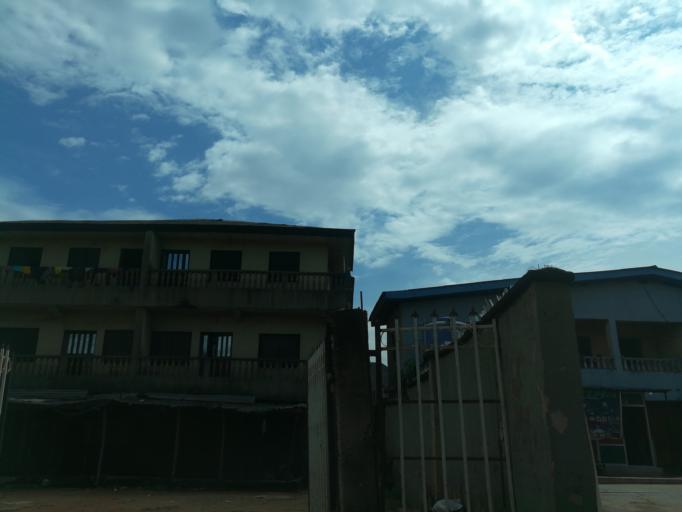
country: NG
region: Lagos
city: Ikorodu
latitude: 6.6060
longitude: 3.5161
